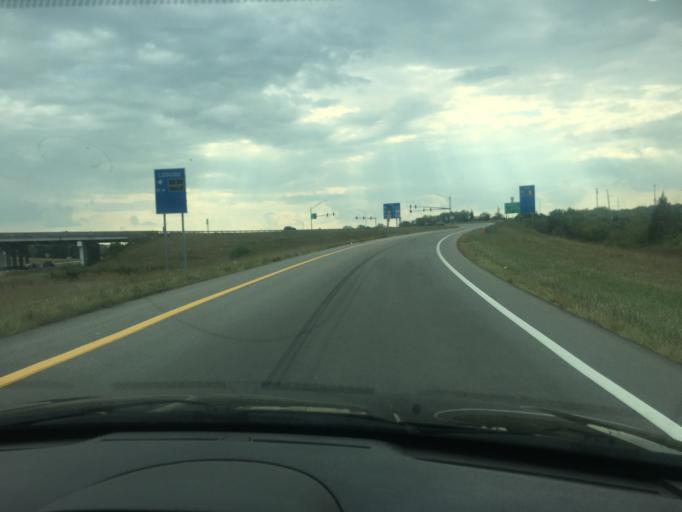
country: US
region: Ohio
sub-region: Clark County
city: Springfield
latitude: 39.9444
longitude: -83.8405
